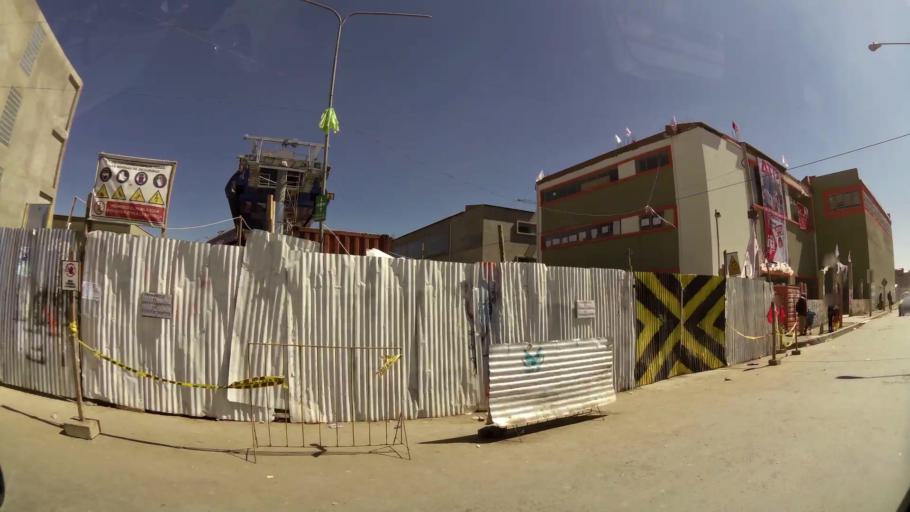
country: BO
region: La Paz
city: La Paz
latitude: -16.4896
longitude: -68.1926
